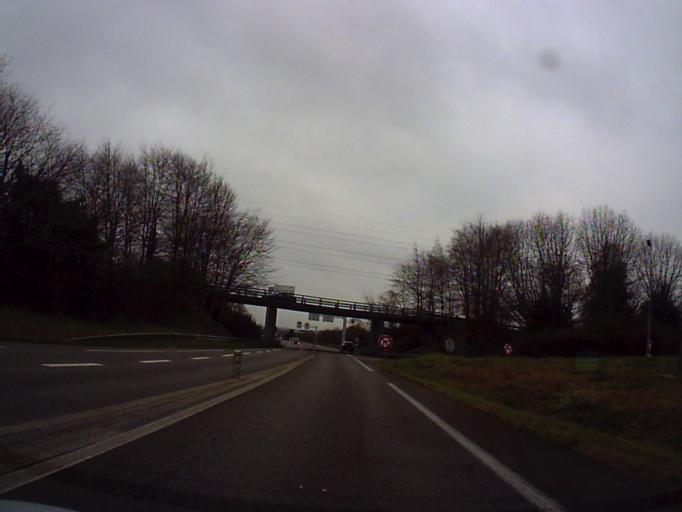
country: FR
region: Brittany
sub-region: Departement du Morbihan
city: Vannes
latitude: 47.6702
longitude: -2.7229
